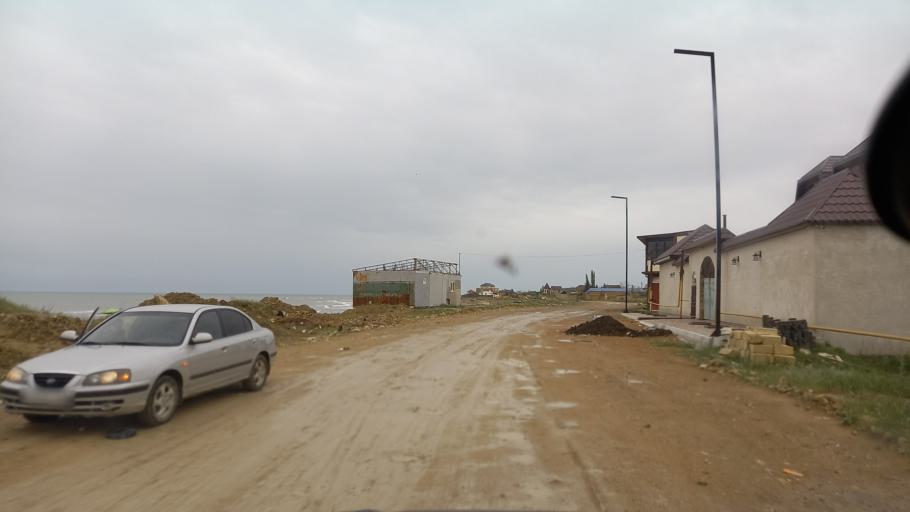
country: RU
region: Dagestan
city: Sabnova
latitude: 42.1201
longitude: 48.2650
